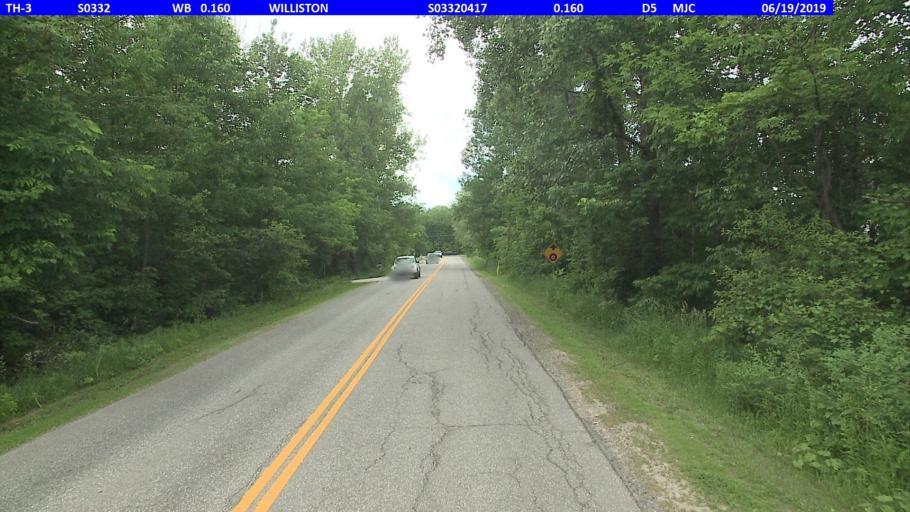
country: US
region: Vermont
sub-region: Chittenden County
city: Williston
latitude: 44.4270
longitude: -73.1184
